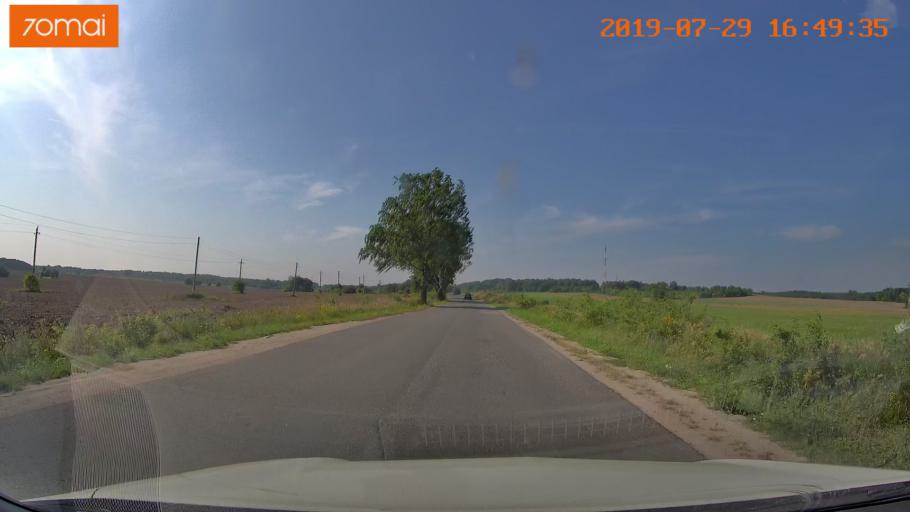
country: RU
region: Kaliningrad
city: Primorsk
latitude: 54.7955
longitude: 20.0640
